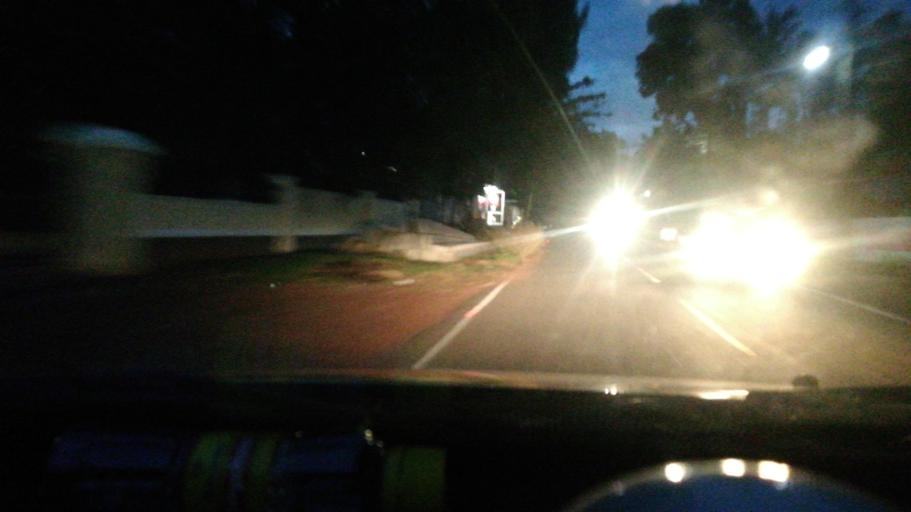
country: IN
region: Kerala
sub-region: Thiruvananthapuram
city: Paravur
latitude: 8.8079
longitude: 76.6894
